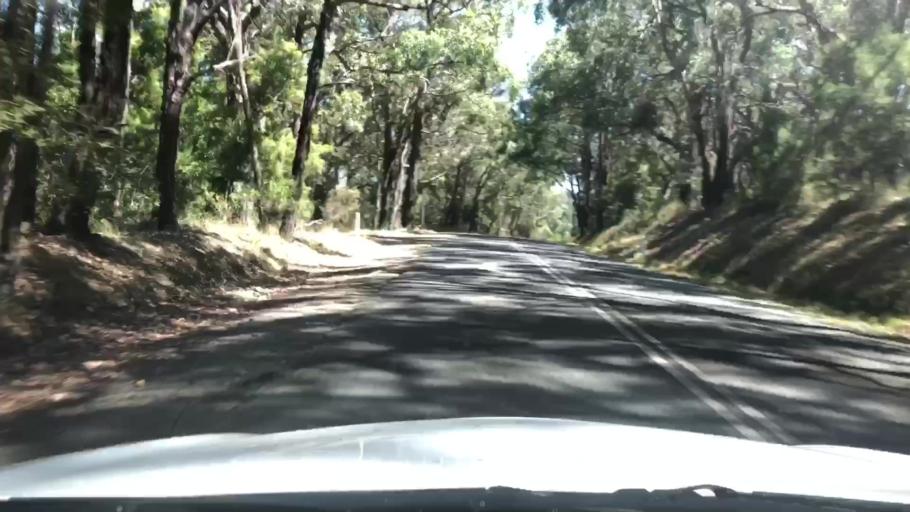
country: AU
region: Victoria
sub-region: Yarra Ranges
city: Macclesfield
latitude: -37.8777
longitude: 145.4777
